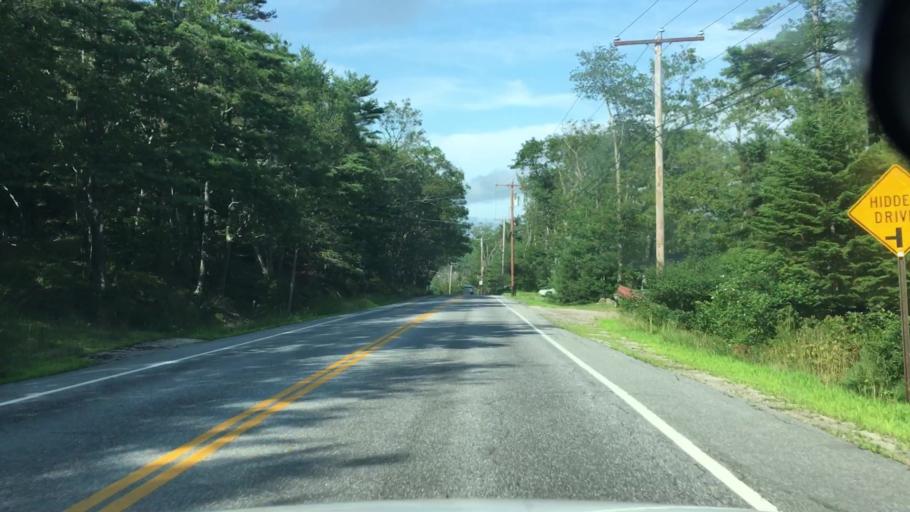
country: US
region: Maine
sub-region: Cumberland County
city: Harpswell Center
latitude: 43.7960
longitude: -69.9364
